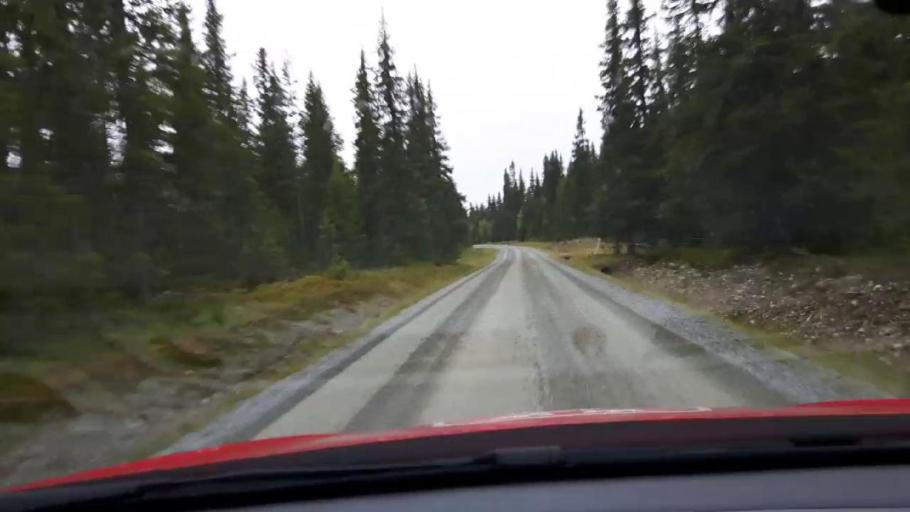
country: SE
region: Jaemtland
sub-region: Bergs Kommun
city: Hoverberg
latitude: 62.8703
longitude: 13.9613
